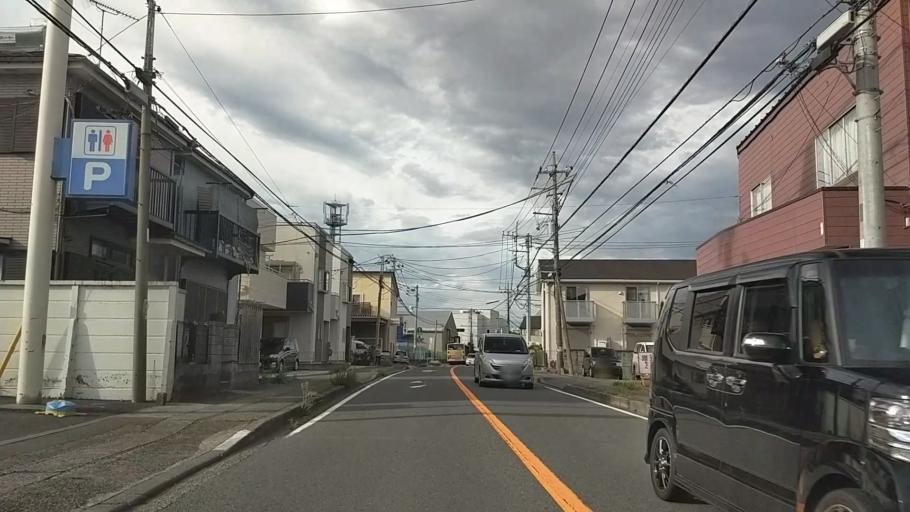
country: JP
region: Kanagawa
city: Zama
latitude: 35.5663
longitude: 139.3407
